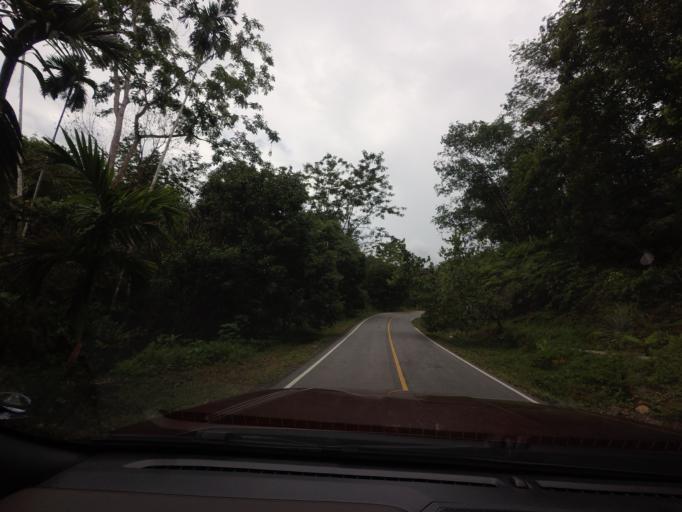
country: TH
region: Narathiwat
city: Sukhirin
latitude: 5.9817
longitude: 101.6824
